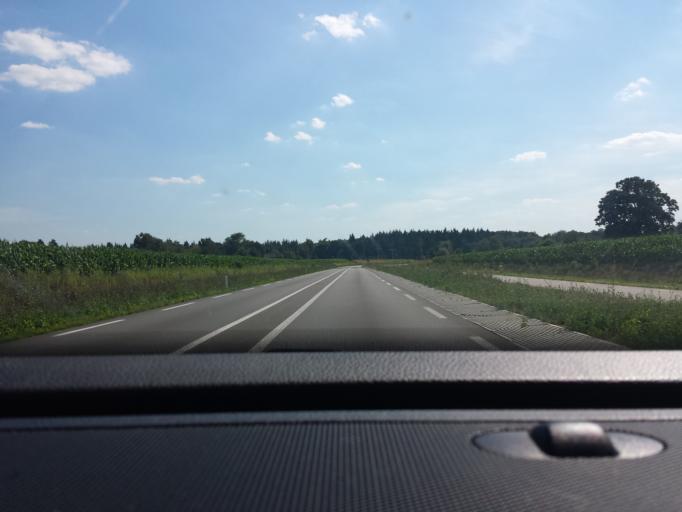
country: NL
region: Gelderland
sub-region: Gemeente Bronckhorst
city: Baak
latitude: 52.0077
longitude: 6.2296
